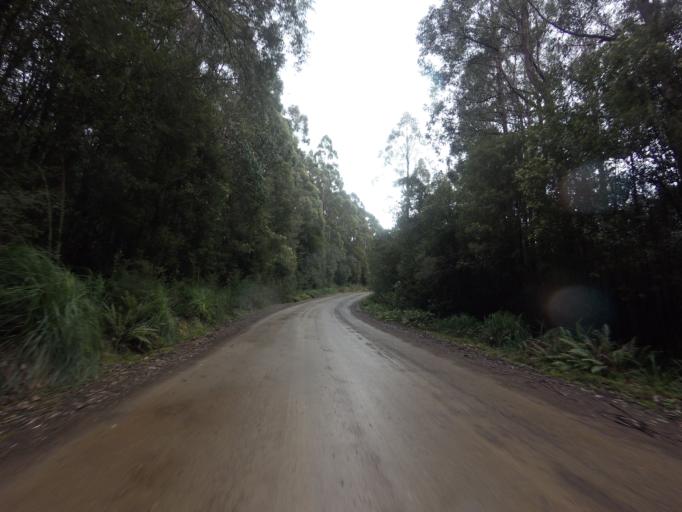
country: AU
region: Tasmania
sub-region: Huon Valley
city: Geeveston
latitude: -43.4792
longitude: 146.8904
